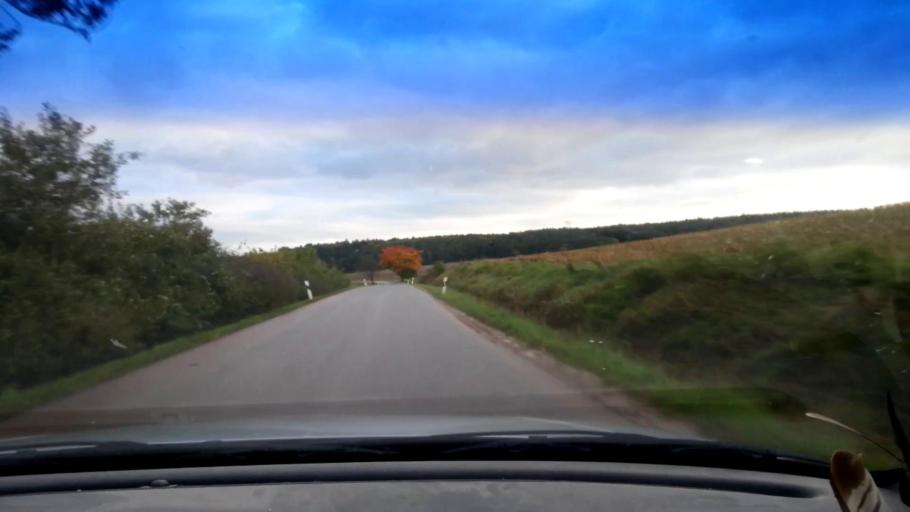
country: DE
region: Bavaria
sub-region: Upper Franconia
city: Burgebrach
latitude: 49.8118
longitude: 10.6912
